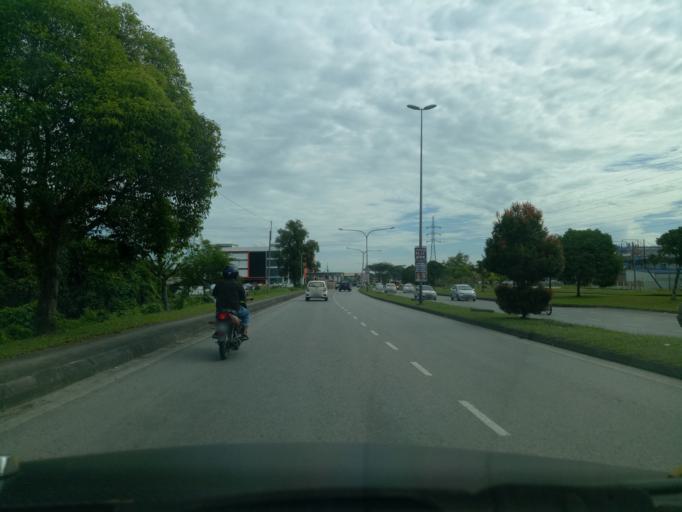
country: MY
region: Sarawak
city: Kuching
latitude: 1.4888
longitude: 110.3307
